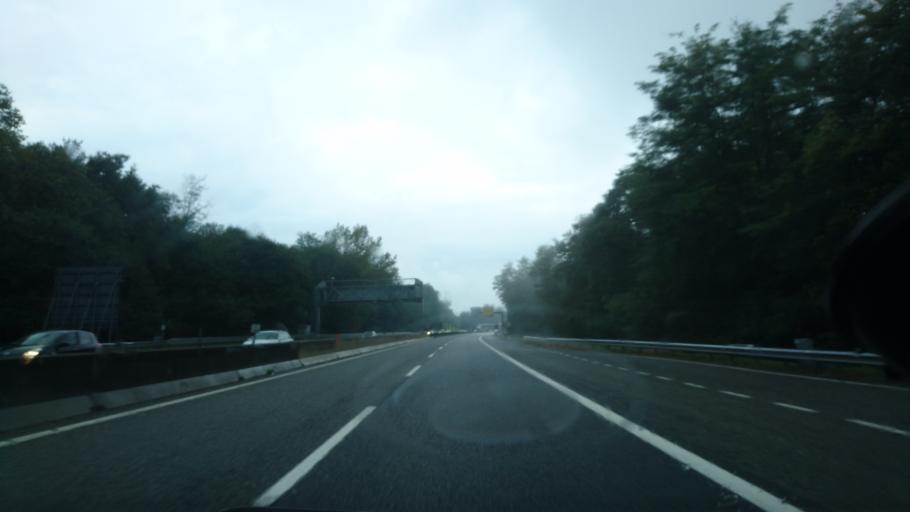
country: IT
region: Piedmont
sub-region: Provincia di Novara
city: Paruzzaro
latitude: 45.7364
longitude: 8.5056
